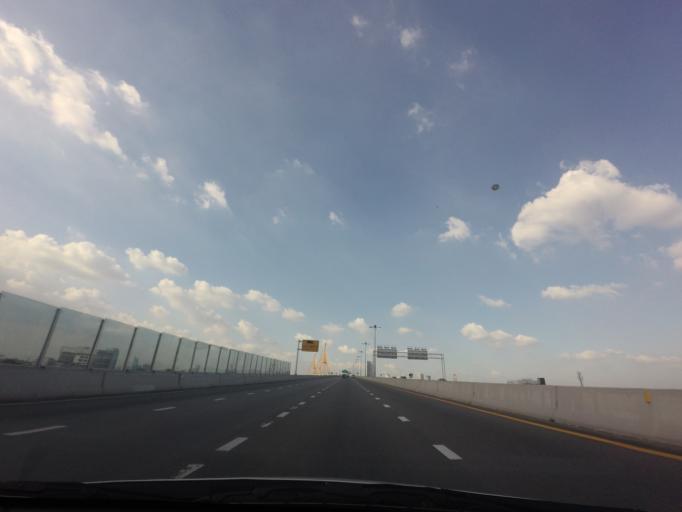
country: TH
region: Samut Prakan
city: Phra Pradaeng
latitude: 13.6492
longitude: 100.5414
